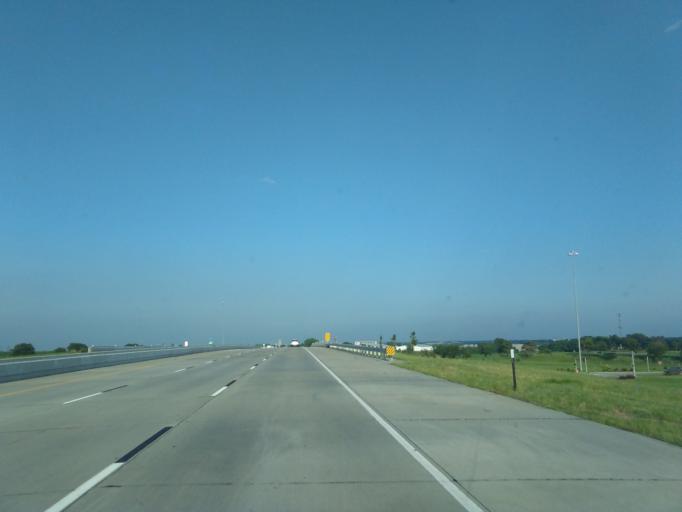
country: US
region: Nebraska
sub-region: Lancaster County
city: Lincoln
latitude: 40.8176
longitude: -96.7895
